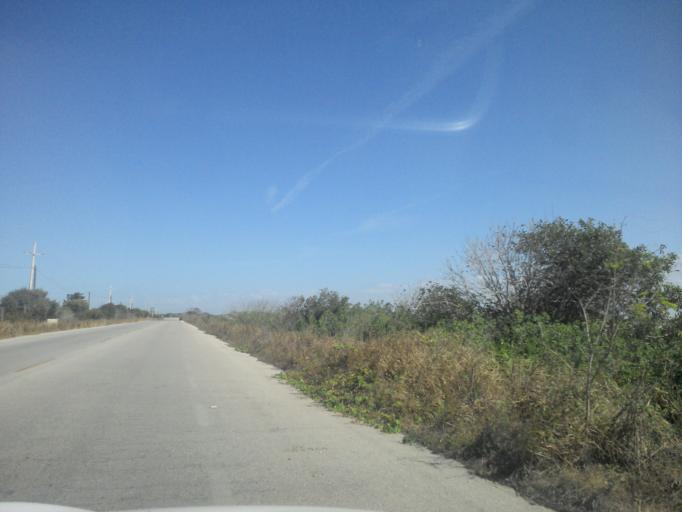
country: MX
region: Yucatan
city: Telchac Puerto
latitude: 21.3286
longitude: -89.3913
